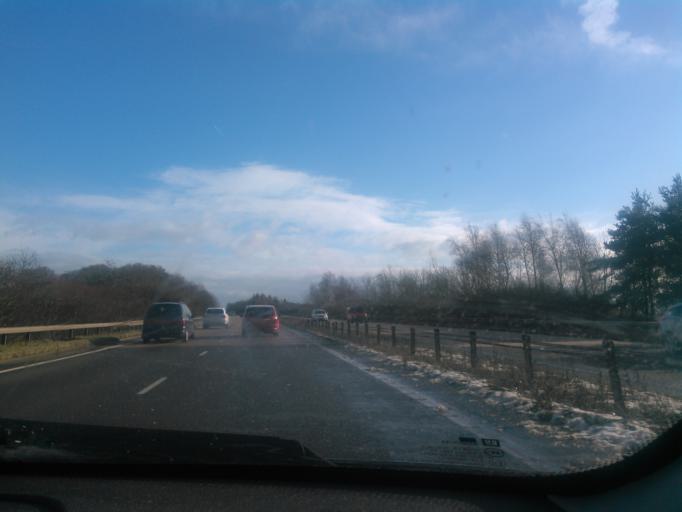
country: GB
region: England
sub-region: Staffordshire
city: Cheadle
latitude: 52.9352
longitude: -1.9764
